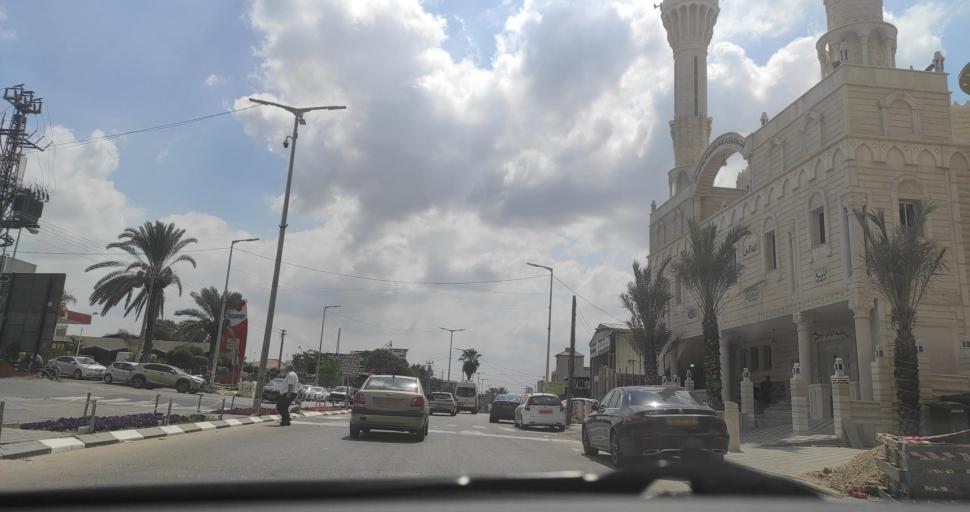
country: IL
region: Central District
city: Kafr Qasim
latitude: 32.1148
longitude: 34.9639
